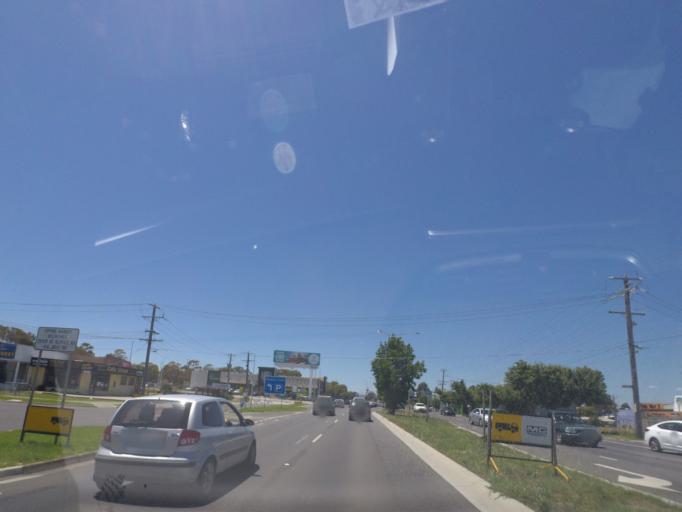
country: AU
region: Victoria
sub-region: Whittlesea
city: Lalor
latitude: -37.6566
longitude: 145.0204
